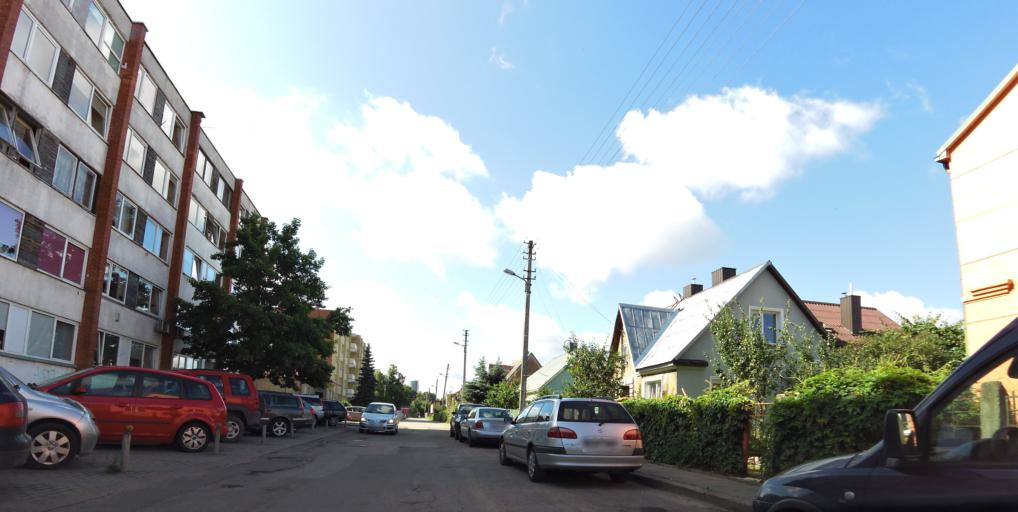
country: LT
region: Vilnius County
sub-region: Vilnius
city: Vilnius
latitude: 54.7095
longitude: 25.2812
